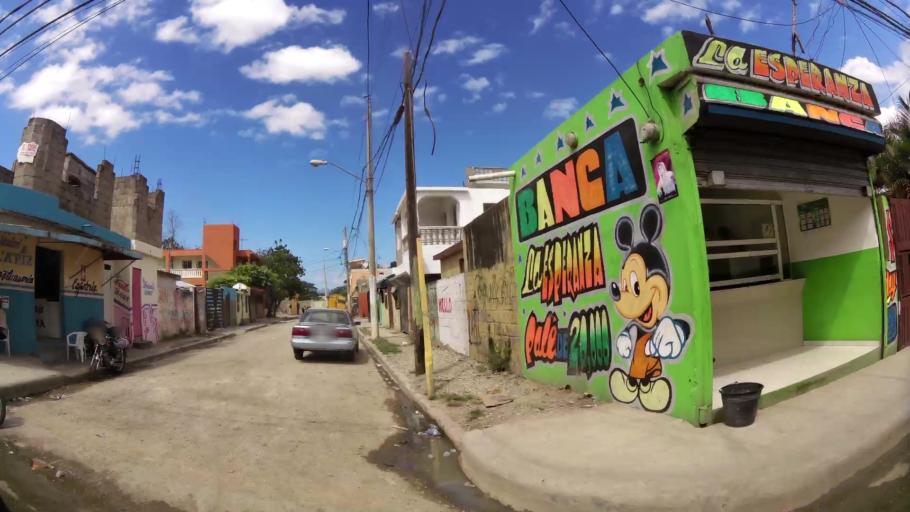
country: DO
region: San Cristobal
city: San Cristobal
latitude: 18.4293
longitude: -70.1258
